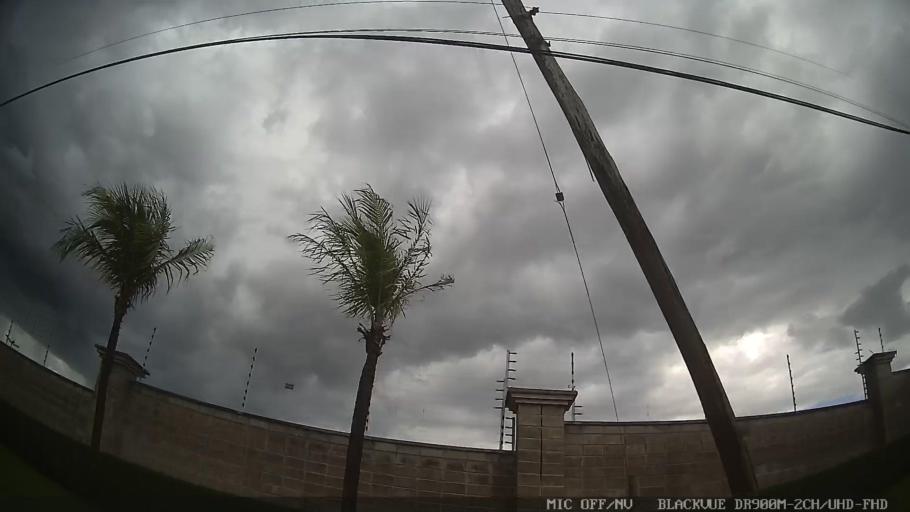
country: BR
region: Sao Paulo
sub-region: Jaguariuna
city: Jaguariuna
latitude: -22.6701
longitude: -46.9664
